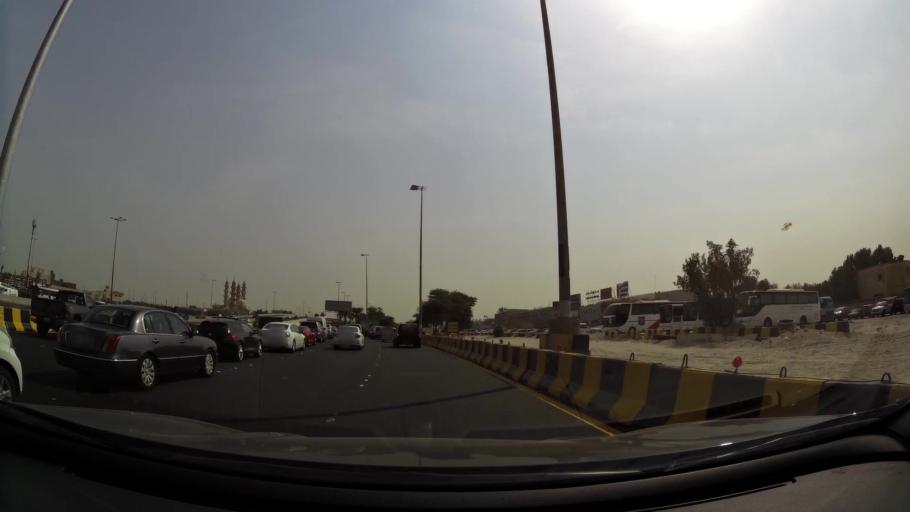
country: KW
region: Al Asimah
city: Ash Shamiyah
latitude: 29.3355
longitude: 47.9499
